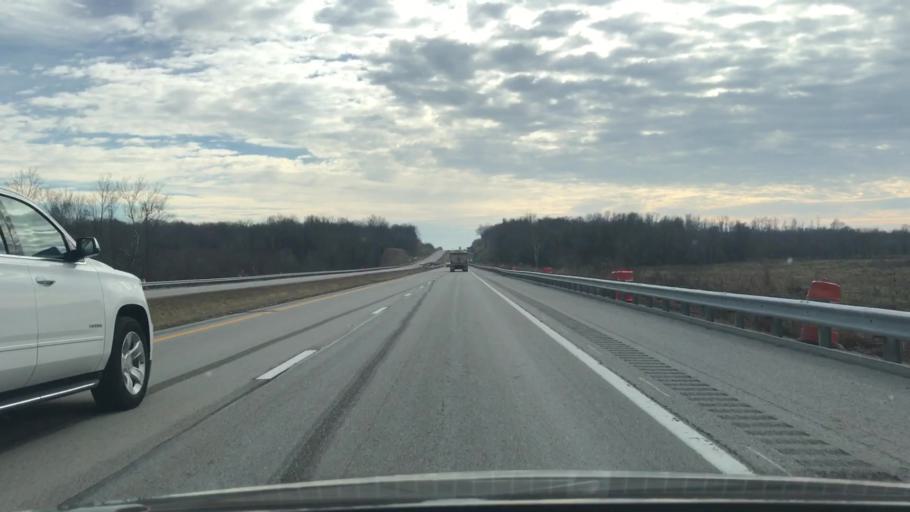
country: US
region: Kentucky
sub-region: Ohio County
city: Hartford
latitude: 37.4787
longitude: -86.9030
